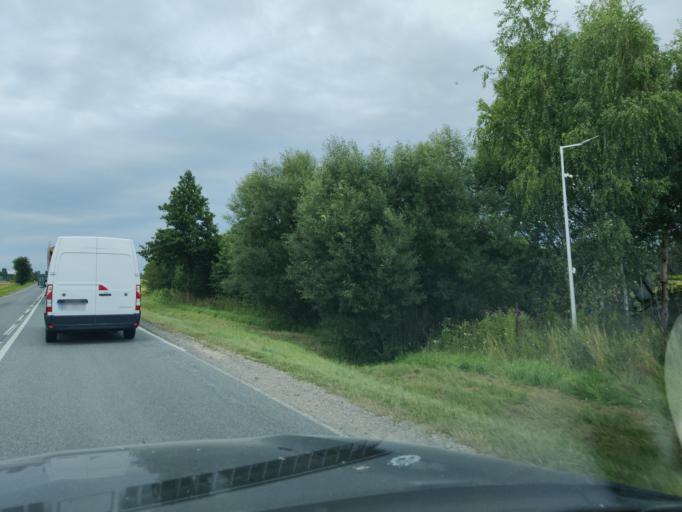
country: PL
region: Masovian Voivodeship
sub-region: Powiat minski
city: Stanislawow
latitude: 52.2329
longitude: 21.5412
